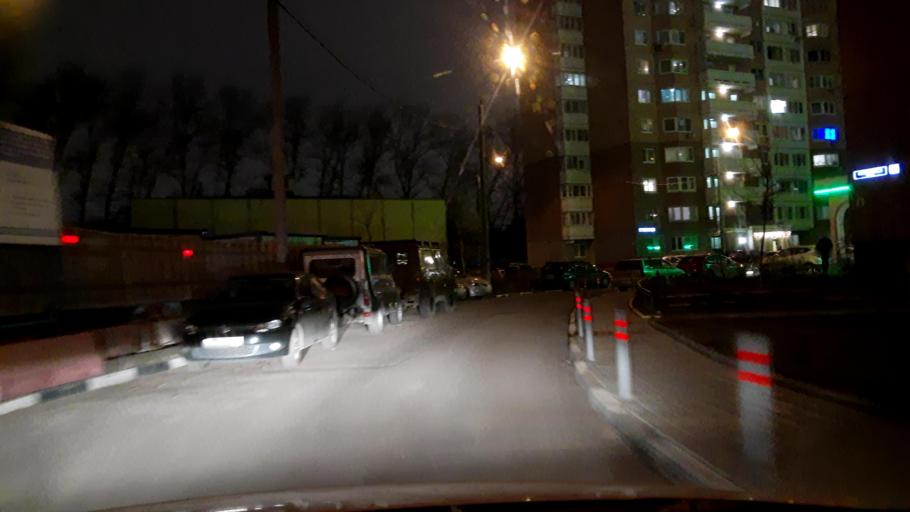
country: RU
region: Moscow
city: Ochakovo-Matveyevskoye
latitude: 55.6865
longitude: 37.4598
